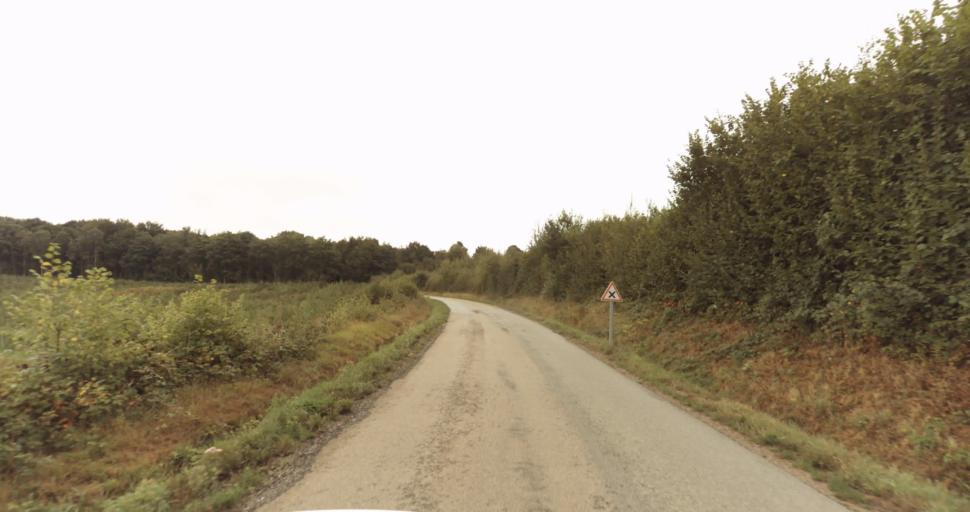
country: FR
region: Lower Normandy
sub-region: Departement de l'Orne
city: Trun
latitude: 48.9054
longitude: 0.1037
